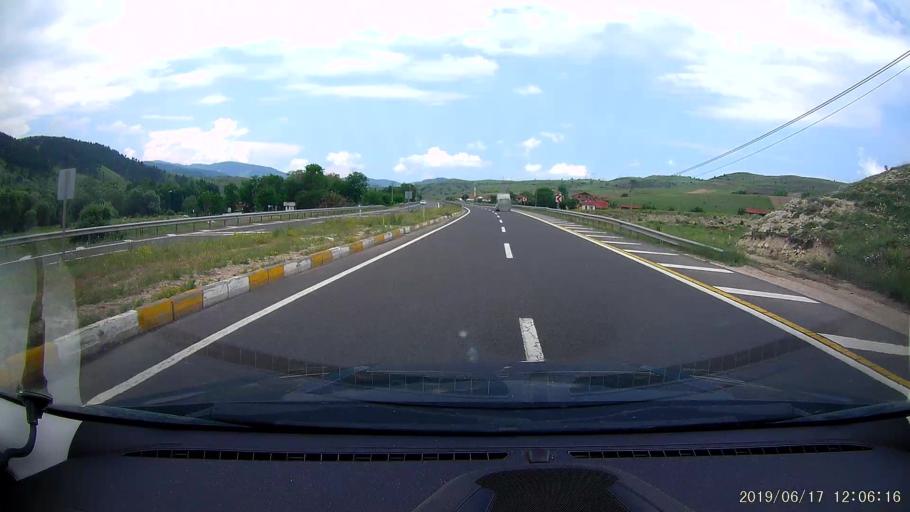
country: TR
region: Cankiri
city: Cerkes
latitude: 40.8424
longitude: 32.7643
